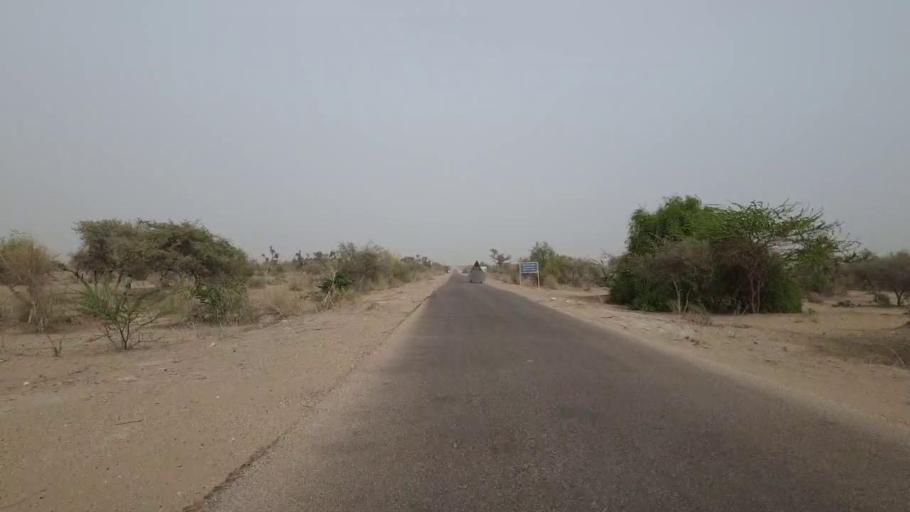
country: PK
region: Sindh
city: Islamkot
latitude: 24.5759
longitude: 70.3123
